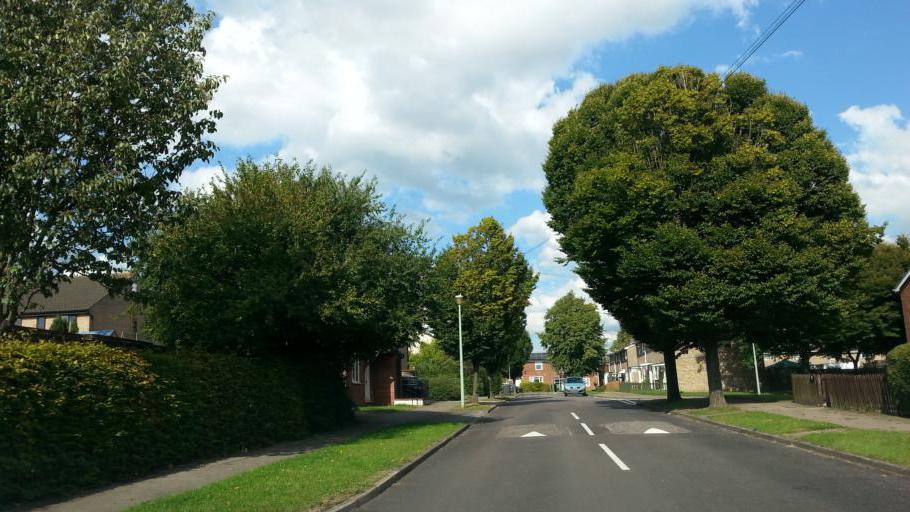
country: GB
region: England
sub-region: Suffolk
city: Bury St Edmunds
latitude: 52.2614
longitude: 0.6935
